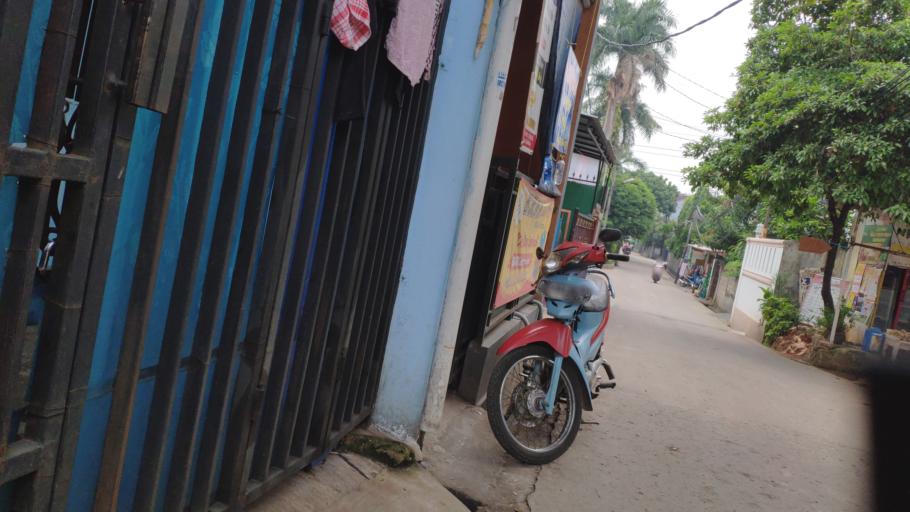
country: ID
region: West Java
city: Depok
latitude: -6.3105
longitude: 106.8283
